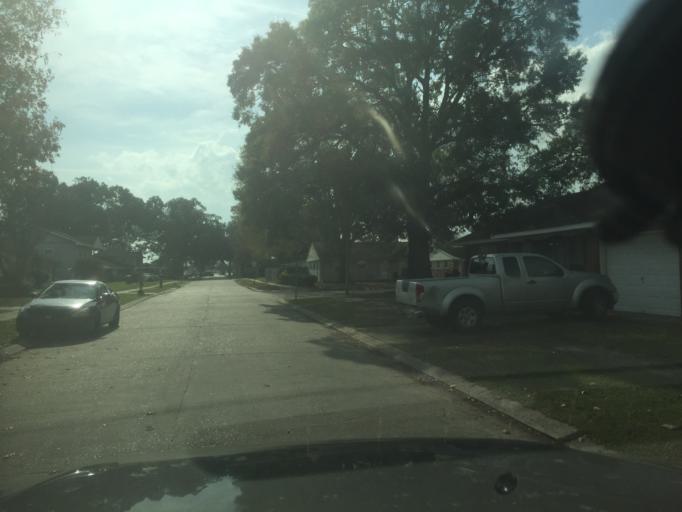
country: US
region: Louisiana
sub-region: Jefferson Parish
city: Avondale
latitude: 29.9134
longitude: -90.2016
